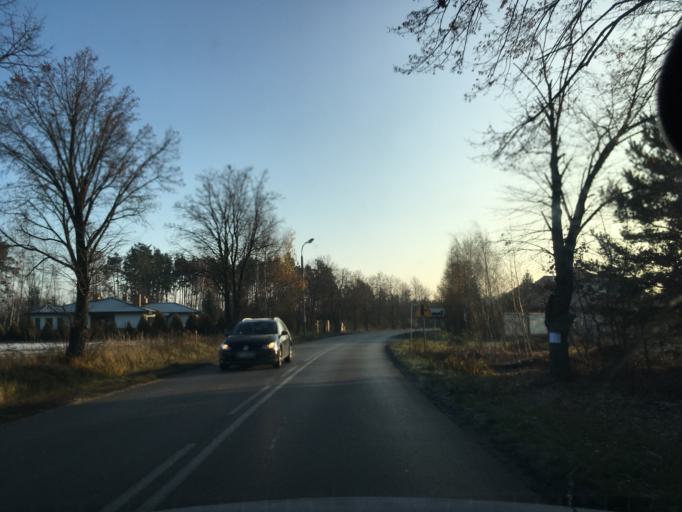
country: PL
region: Masovian Voivodeship
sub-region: Powiat piaseczynski
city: Lesznowola
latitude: 52.0744
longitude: 20.9705
